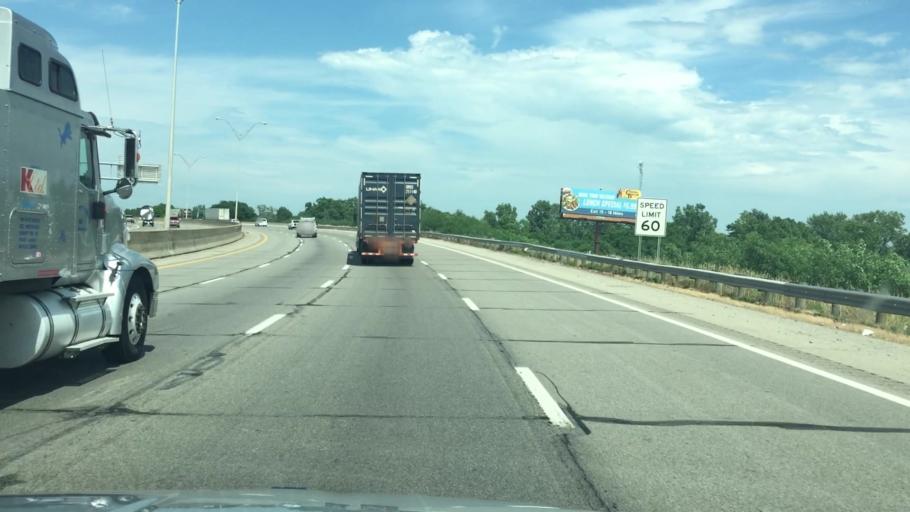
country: US
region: Ohio
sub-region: Lucas County
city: Oregon
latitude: 41.6924
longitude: -83.5054
